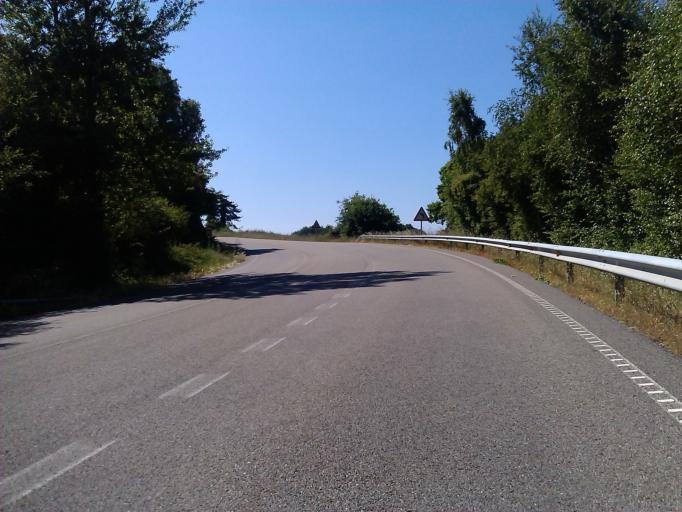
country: ES
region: Galicia
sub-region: Provincia de Lugo
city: Samos
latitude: 42.7342
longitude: -7.3556
